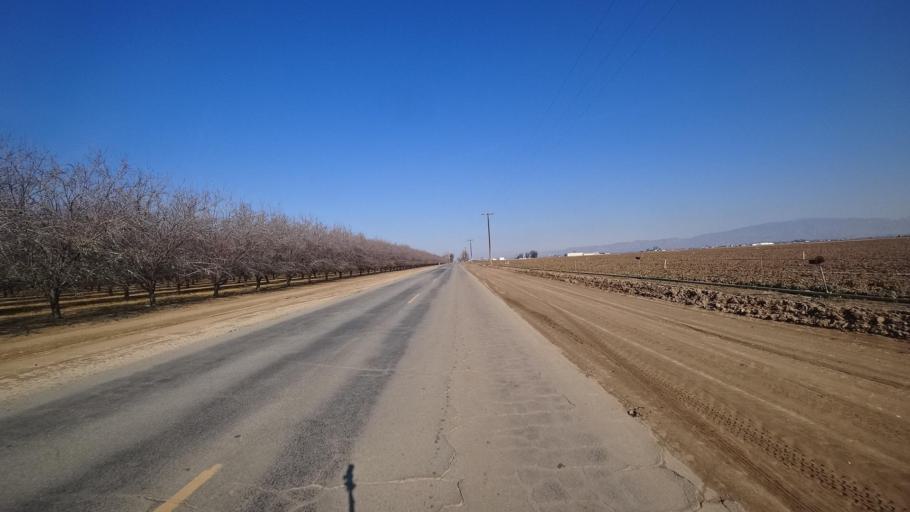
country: US
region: California
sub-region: Kern County
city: Weedpatch
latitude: 35.2406
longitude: -118.8962
